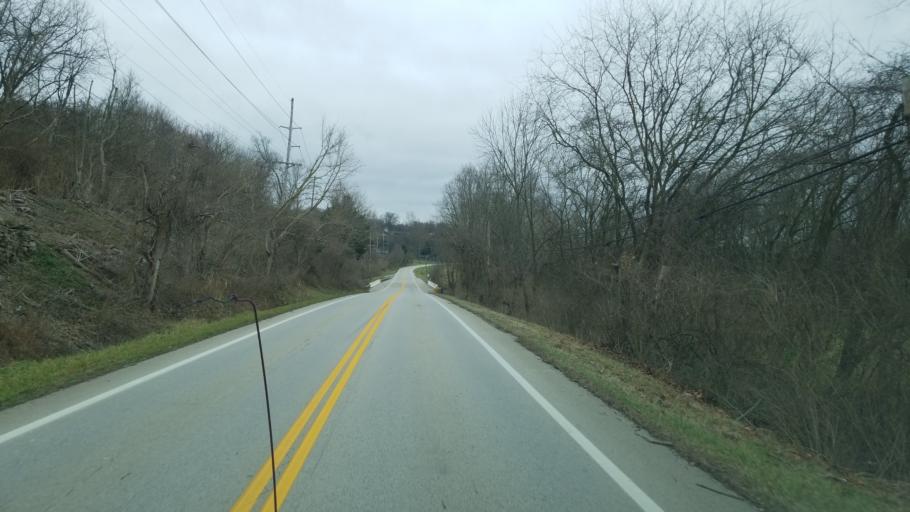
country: US
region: Ohio
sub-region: Clermont County
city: New Richmond
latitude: 38.9272
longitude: -84.2579
